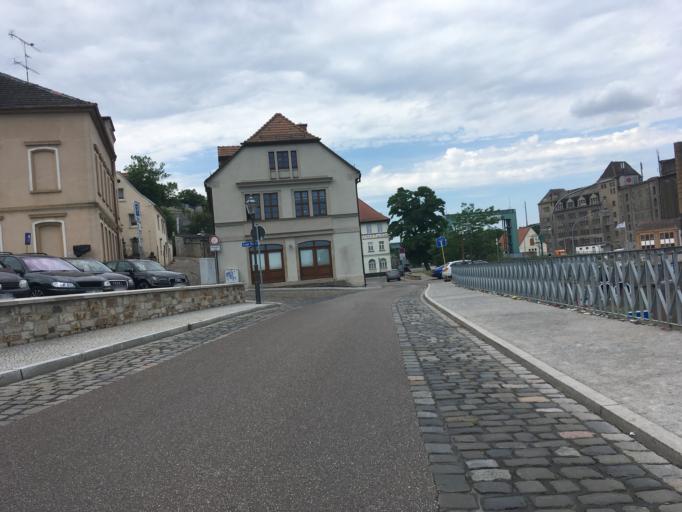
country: DE
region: Saxony-Anhalt
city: Bernburg
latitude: 51.7971
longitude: 11.7374
